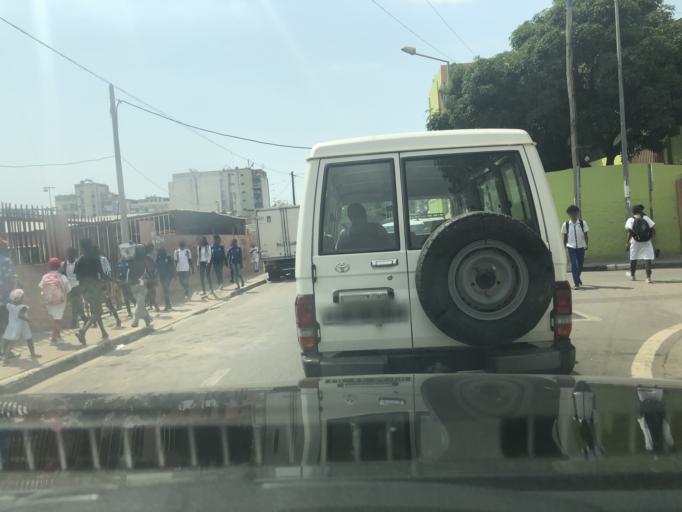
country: AO
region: Luanda
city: Luanda
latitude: -8.8243
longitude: 13.2500
